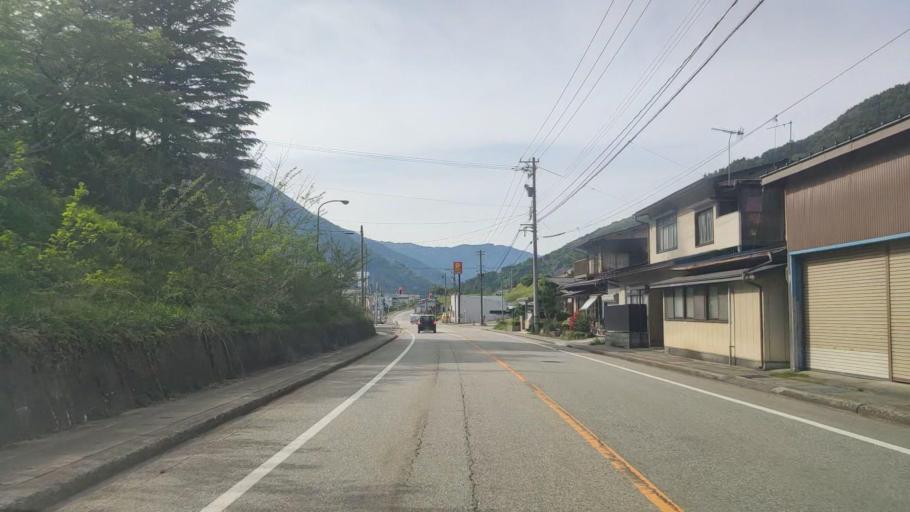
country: JP
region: Gifu
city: Takayama
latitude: 36.3229
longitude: 137.3111
